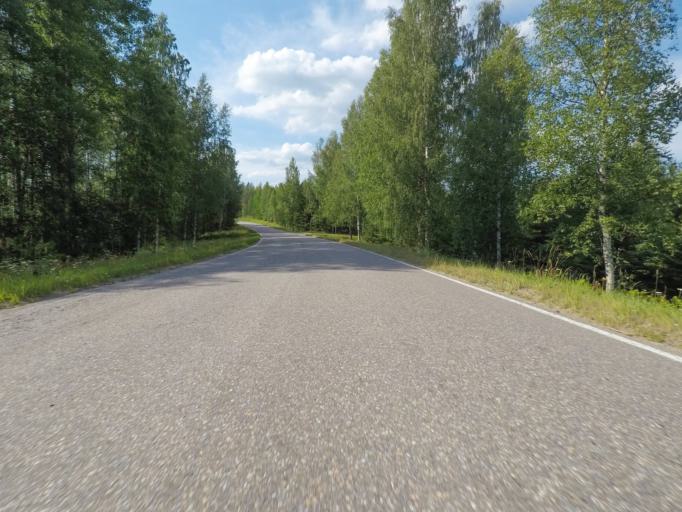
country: FI
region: Southern Savonia
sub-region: Mikkeli
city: Puumala
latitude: 61.6876
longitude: 28.2234
